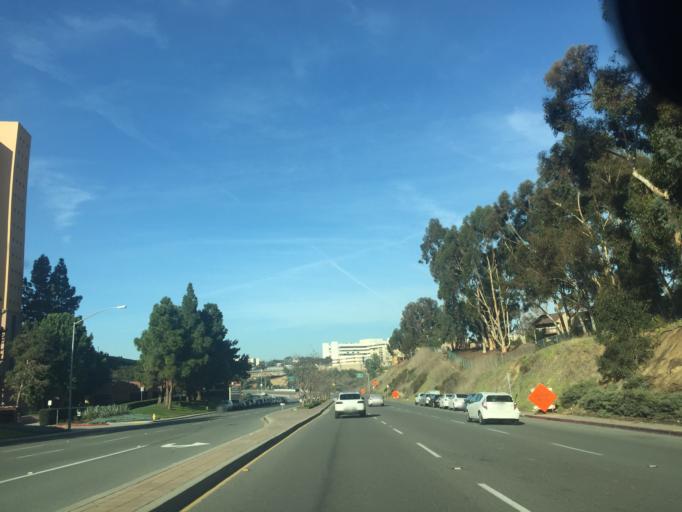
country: US
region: California
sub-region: San Diego County
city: La Jolla
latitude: 32.8711
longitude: -117.2239
